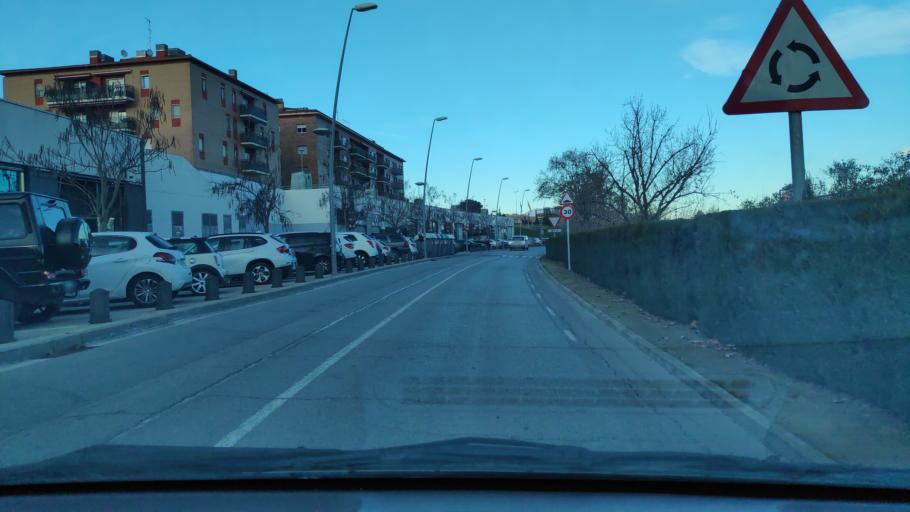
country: ES
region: Catalonia
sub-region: Provincia de Barcelona
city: Montmelo
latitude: 41.5568
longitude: 2.2521
